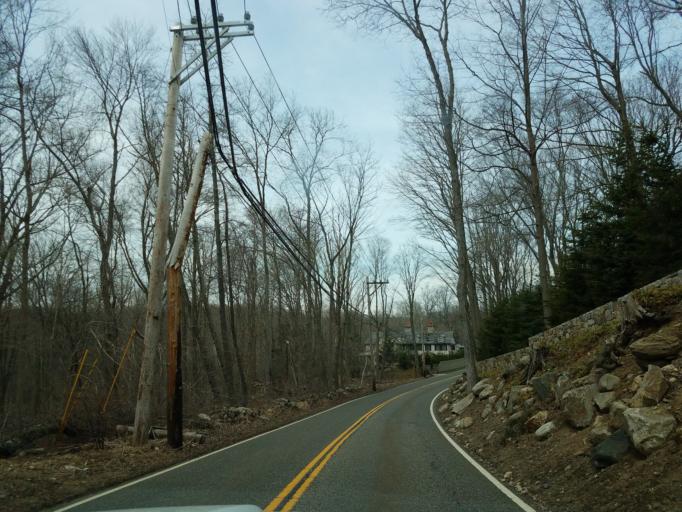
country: US
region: New York
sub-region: Westchester County
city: Armonk
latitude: 41.1028
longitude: -73.6516
